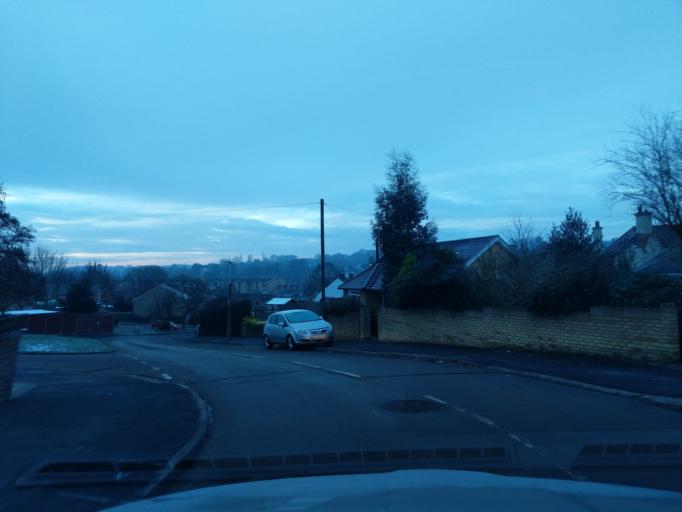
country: GB
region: England
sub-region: Hertfordshire
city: Hemel Hempstead
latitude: 51.7370
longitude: -0.4602
